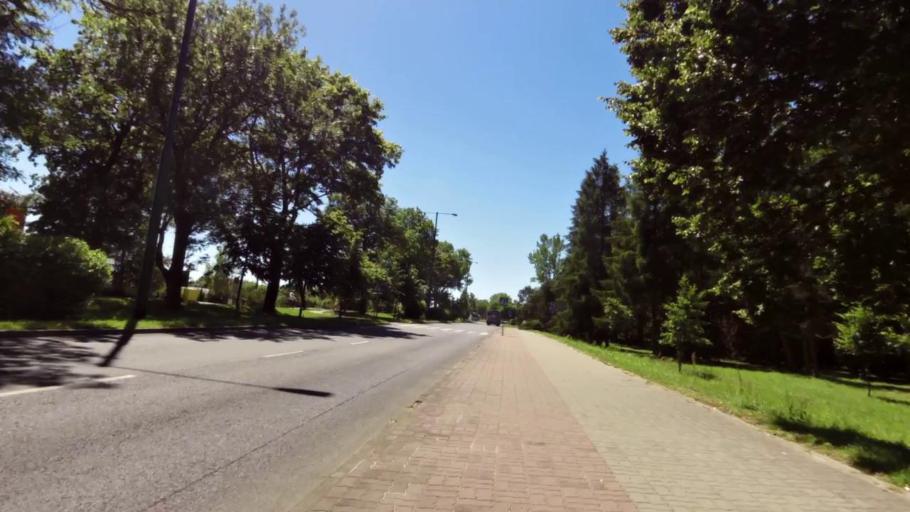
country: PL
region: West Pomeranian Voivodeship
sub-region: Powiat kolobrzeski
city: Kolobrzeg
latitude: 54.1566
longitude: 15.5649
